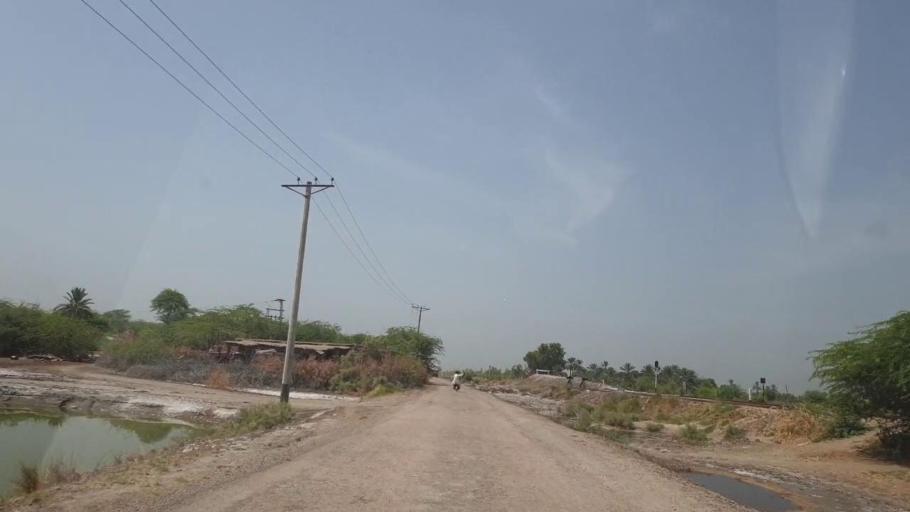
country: PK
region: Sindh
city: Gambat
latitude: 27.3358
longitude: 68.5435
